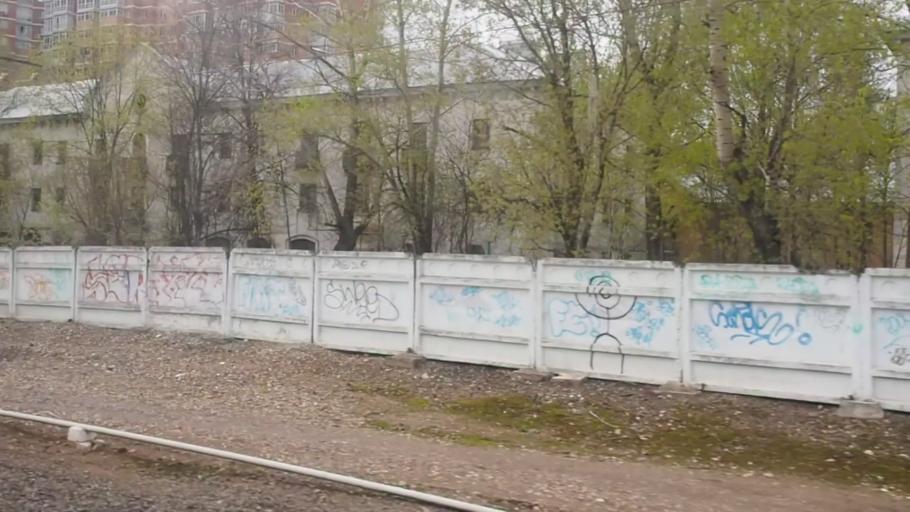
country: RU
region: Moskovskaya
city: Odintsovo
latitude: 55.6777
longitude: 37.2927
